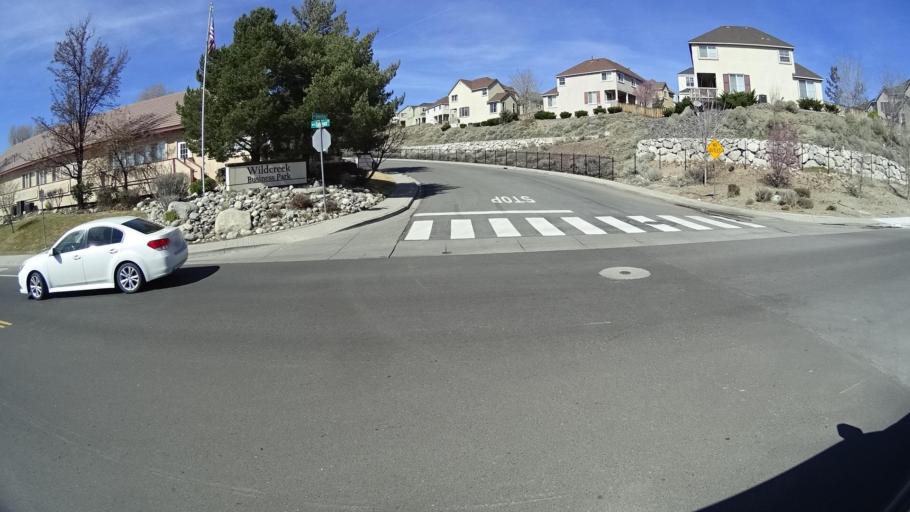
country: US
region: Nevada
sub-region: Washoe County
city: Sparks
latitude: 39.5593
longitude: -119.7718
